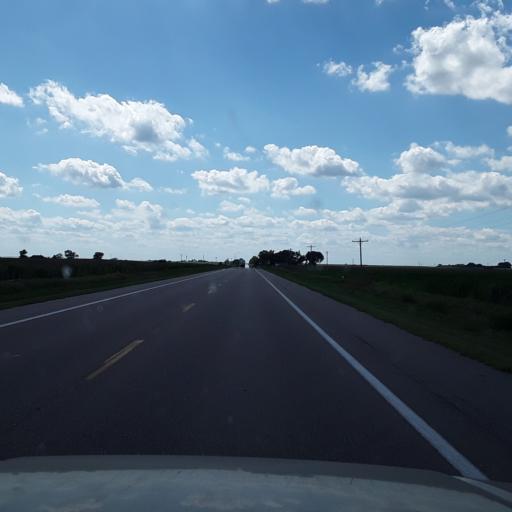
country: US
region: Nebraska
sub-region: Merrick County
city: Central City
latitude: 41.1910
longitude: -97.9936
